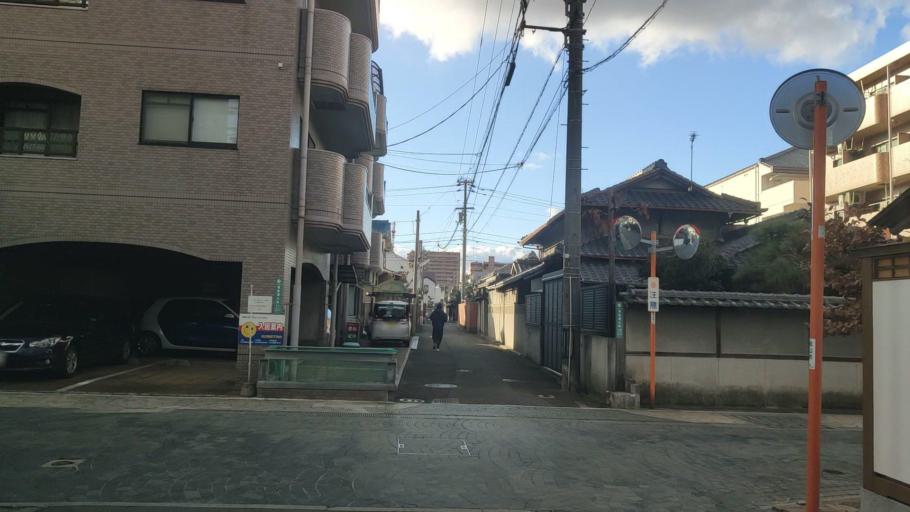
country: JP
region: Ehime
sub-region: Shikoku-chuo Shi
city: Matsuyama
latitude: 33.8516
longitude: 132.7834
